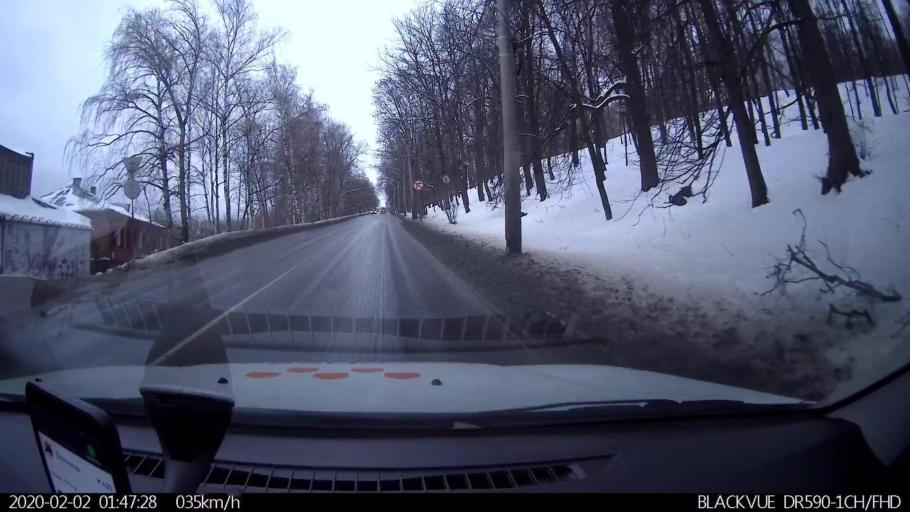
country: RU
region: Nizjnij Novgorod
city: Nizhniy Novgorod
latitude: 56.3337
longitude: 44.0290
